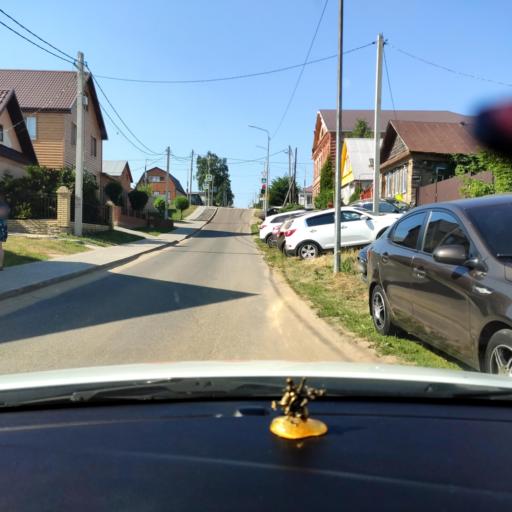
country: RU
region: Tatarstan
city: Laishevo
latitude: 55.3972
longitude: 49.5458
